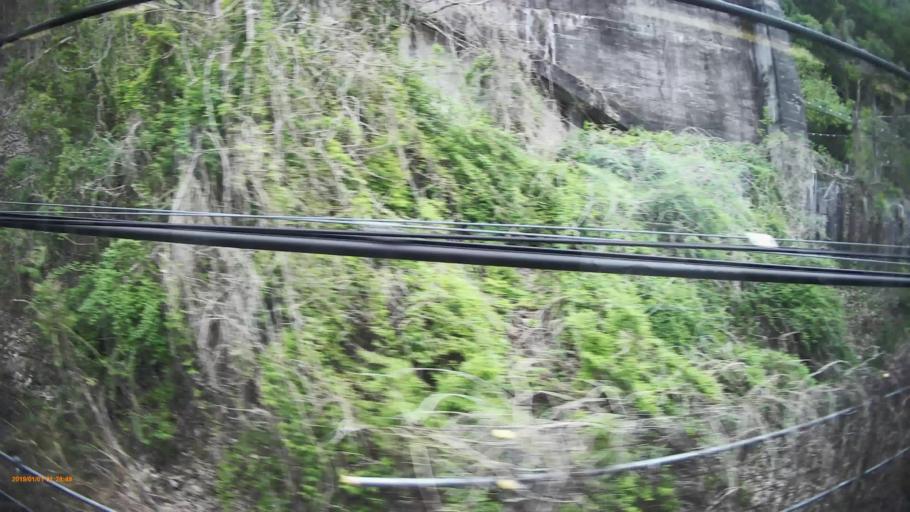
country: JP
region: Yamanashi
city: Enzan
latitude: 35.6893
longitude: 138.7426
